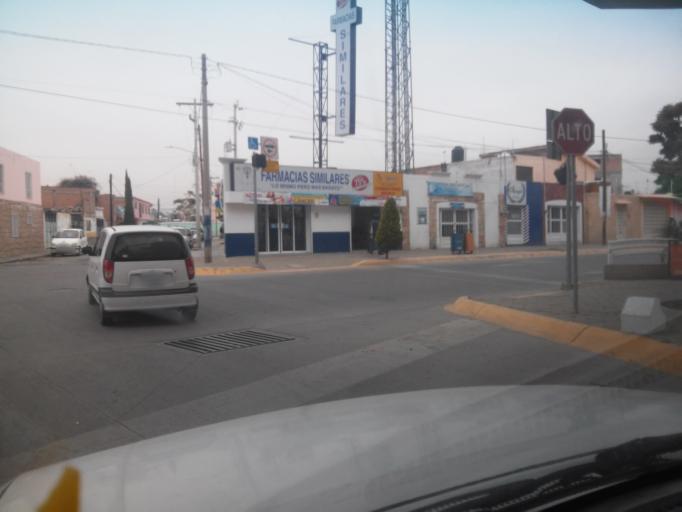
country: MX
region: Durango
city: Victoria de Durango
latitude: 24.0354
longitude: -104.6830
